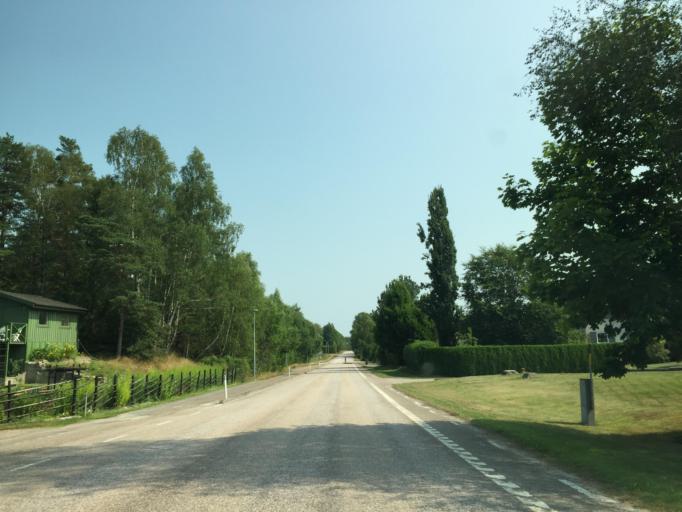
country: SE
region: Vaestra Goetaland
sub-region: Trollhattan
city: Sjuntorp
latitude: 58.3311
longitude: 12.1422
